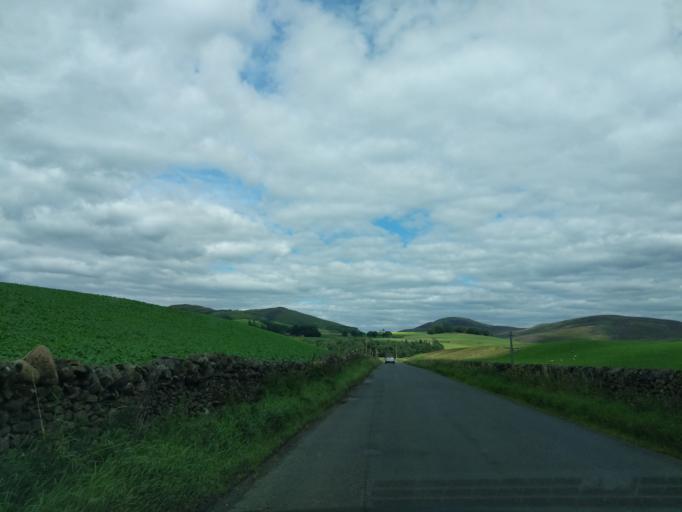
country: GB
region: Scotland
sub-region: The Scottish Borders
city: Peebles
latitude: 55.6457
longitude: -3.2769
